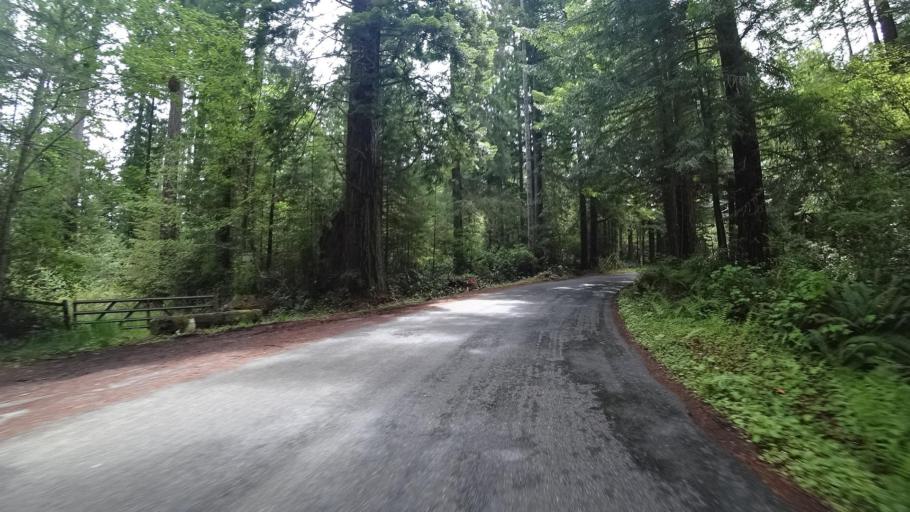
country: US
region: California
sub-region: Humboldt County
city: Bayside
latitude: 40.8552
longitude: -124.0326
